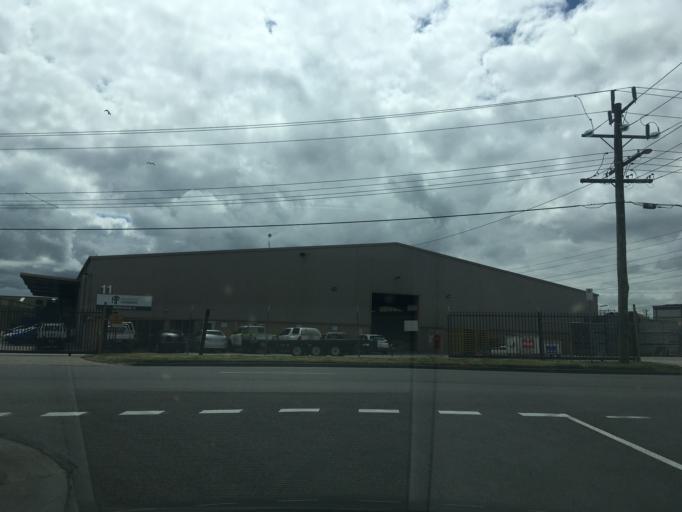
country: AU
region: Victoria
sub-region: Brimbank
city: Brooklyn
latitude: -37.8212
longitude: 144.8148
